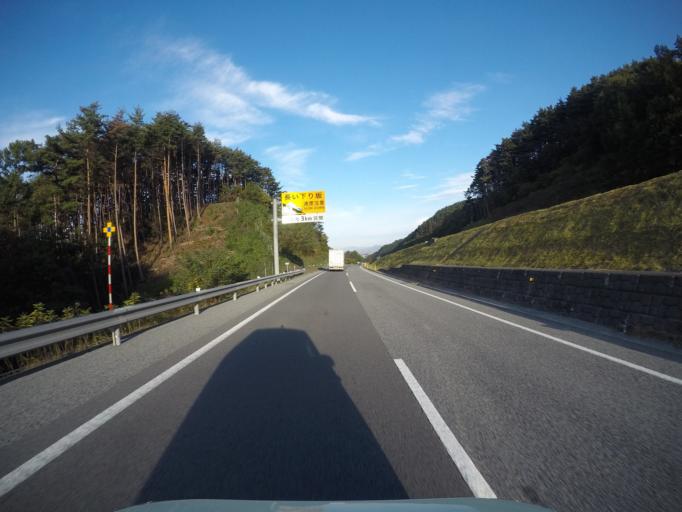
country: JP
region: Nagano
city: Saku
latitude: 36.2709
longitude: 138.5212
